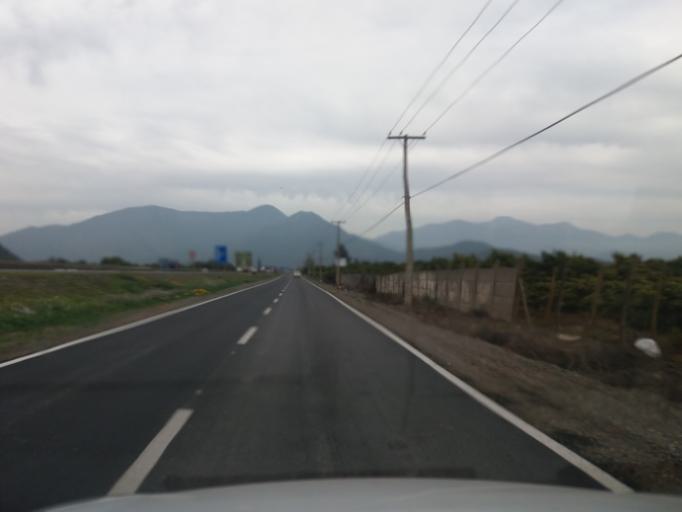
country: CL
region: Valparaiso
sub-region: Provincia de Quillota
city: Hacienda La Calera
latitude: -32.8362
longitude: -71.1184
